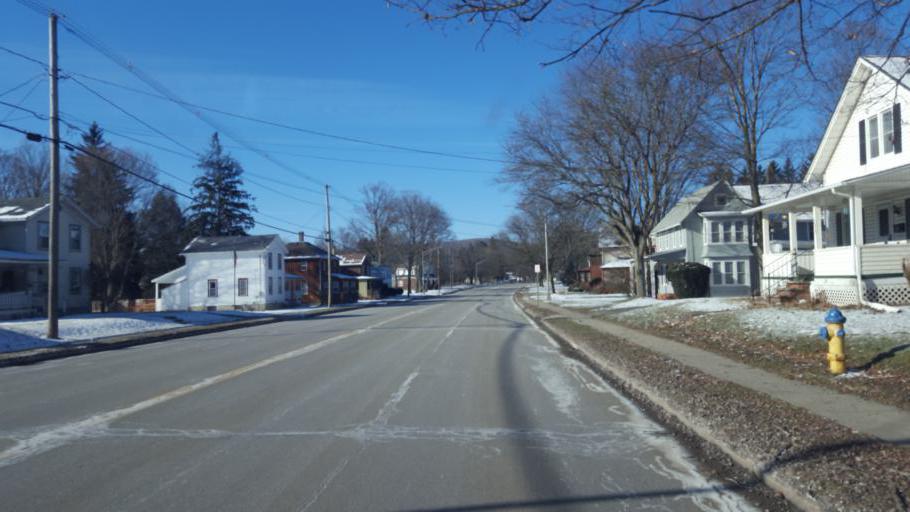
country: US
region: New York
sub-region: Allegany County
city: Wellsville
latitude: 42.1201
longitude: -77.9318
